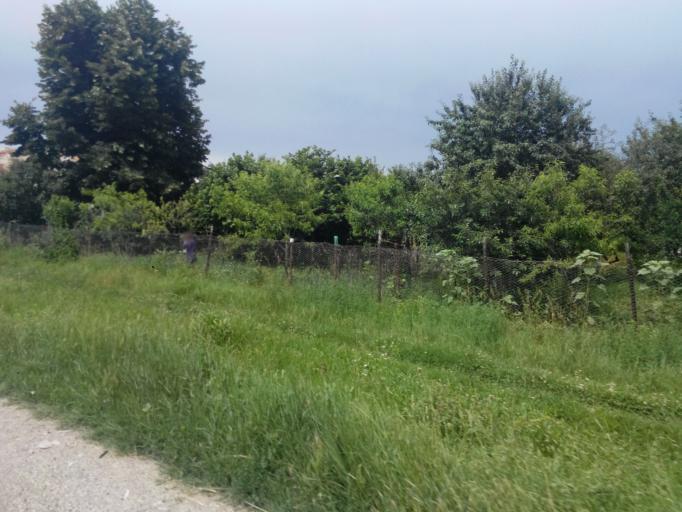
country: RO
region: Arges
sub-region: Comuna Budeasa
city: Galasesti
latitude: 44.9344
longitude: 24.7782
